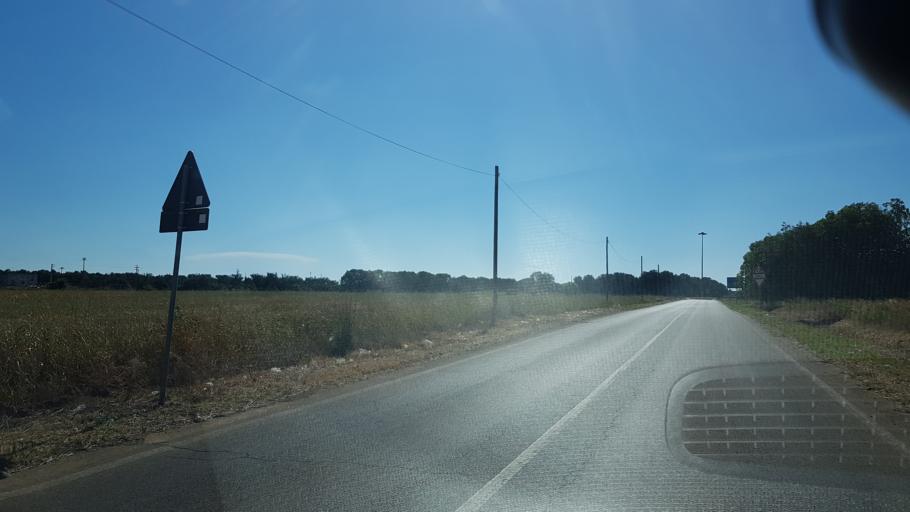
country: IT
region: Apulia
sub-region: Provincia di Brindisi
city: Mesagne
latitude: 40.5574
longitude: 17.8404
